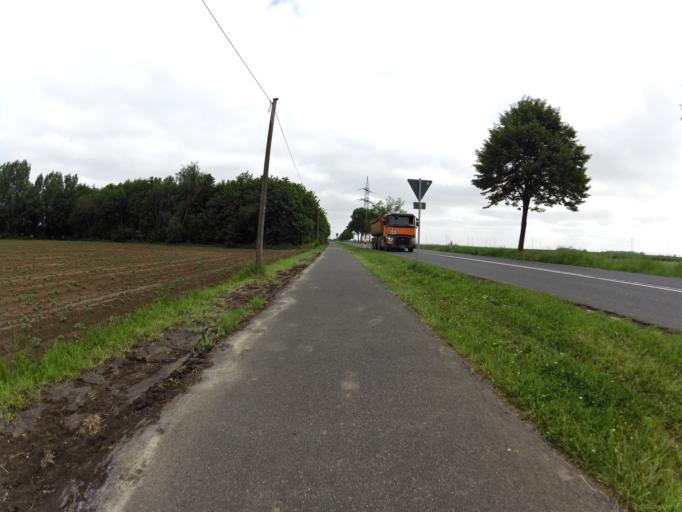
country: DE
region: North Rhine-Westphalia
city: Siersdorf
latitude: 50.9072
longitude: 6.2350
